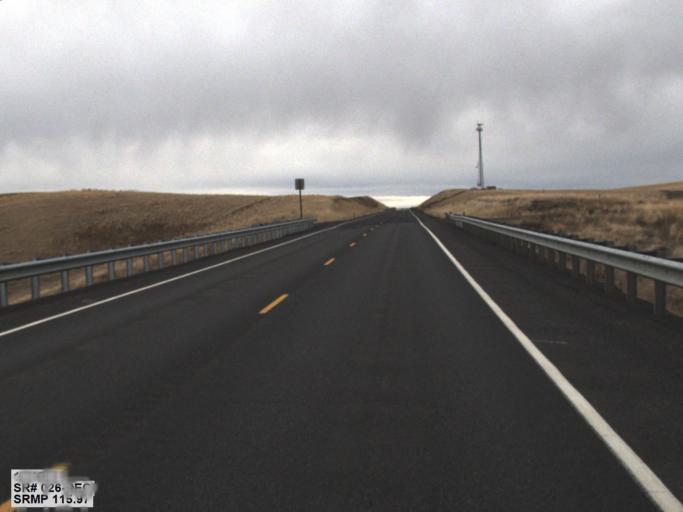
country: US
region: Washington
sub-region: Whitman County
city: Colfax
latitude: 46.8127
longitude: -117.6725
